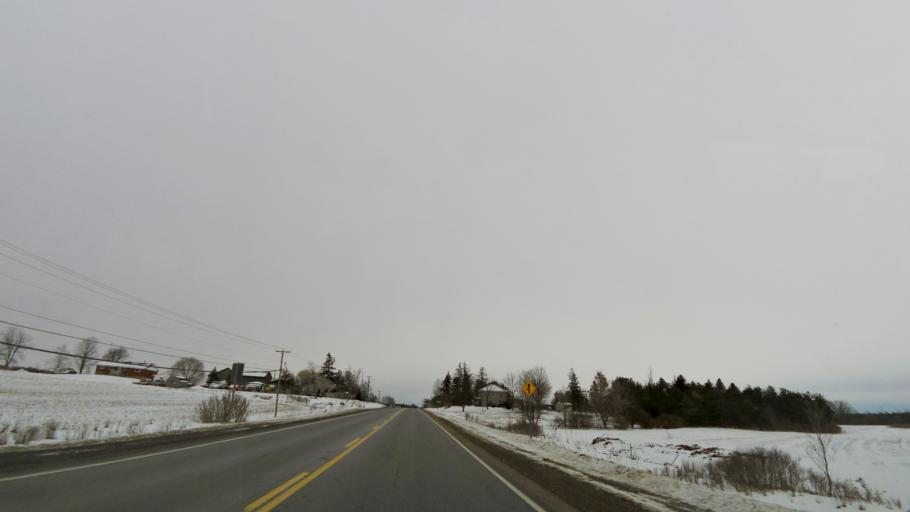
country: CA
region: Ontario
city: Cambridge
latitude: 43.3189
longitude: -80.1837
